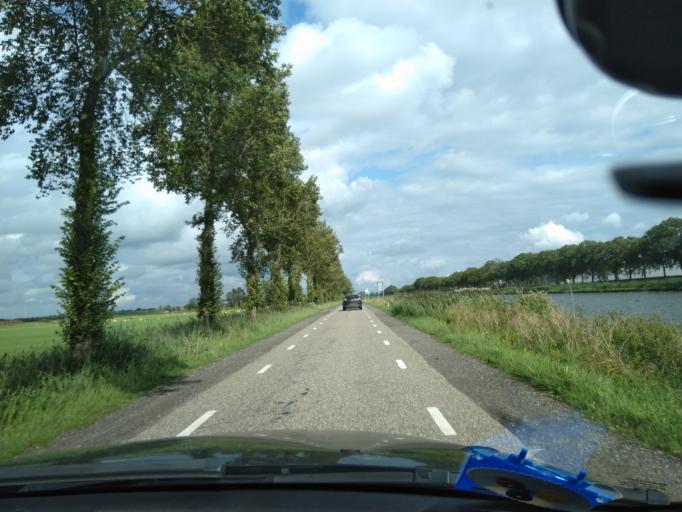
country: NL
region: Groningen
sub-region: Gemeente Zuidhorn
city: Grijpskerk
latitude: 53.2513
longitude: 6.3322
